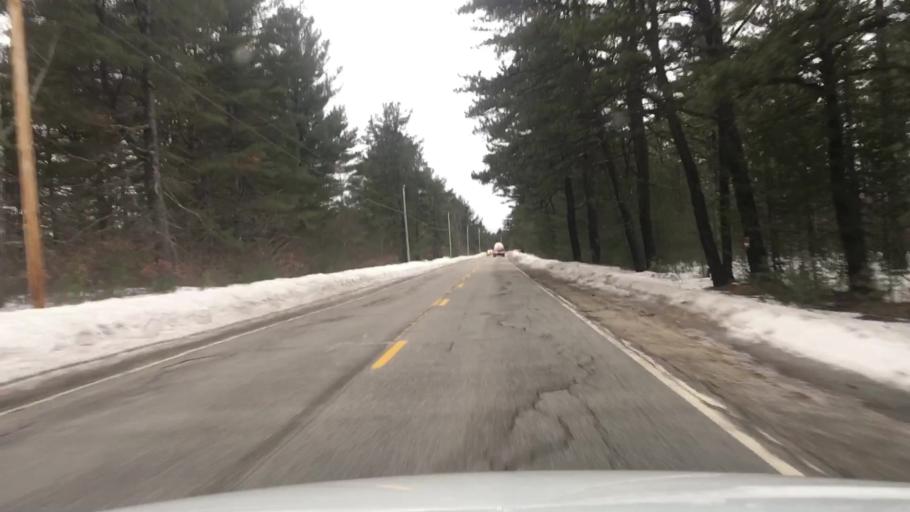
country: US
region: Maine
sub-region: York County
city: Shapleigh
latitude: 43.5690
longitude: -70.8602
